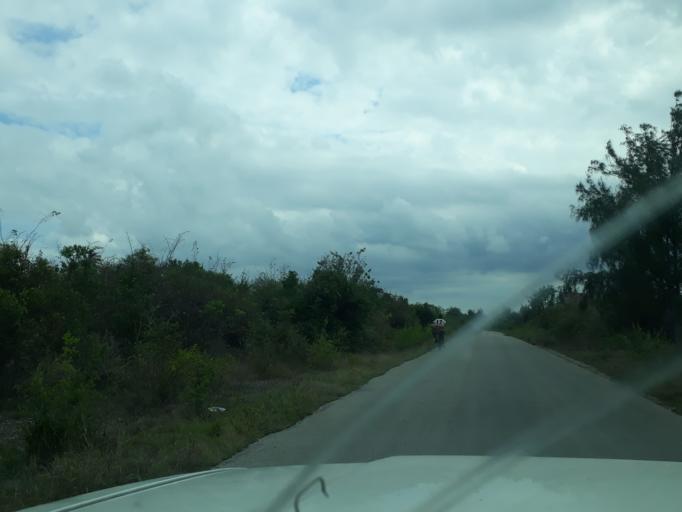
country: TZ
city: Kiwengwa
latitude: -6.0837
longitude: 39.4252
